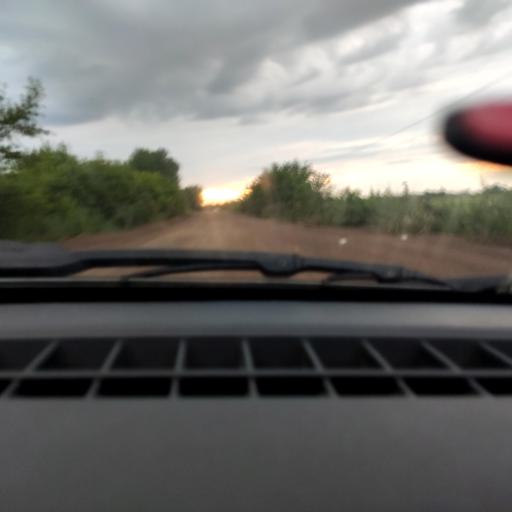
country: RU
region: Bashkortostan
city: Blagoveshchensk
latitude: 54.9178
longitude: 55.9818
